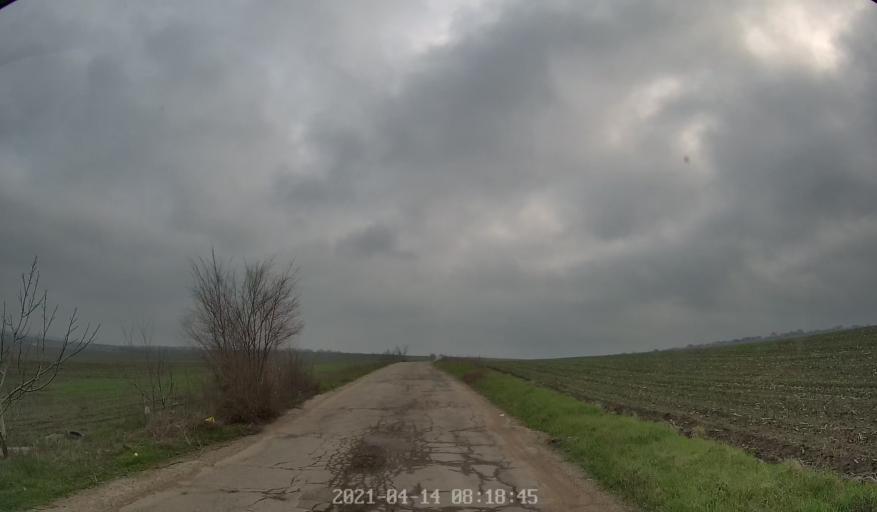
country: MD
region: Chisinau
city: Stauceni
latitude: 47.0573
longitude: 28.9177
